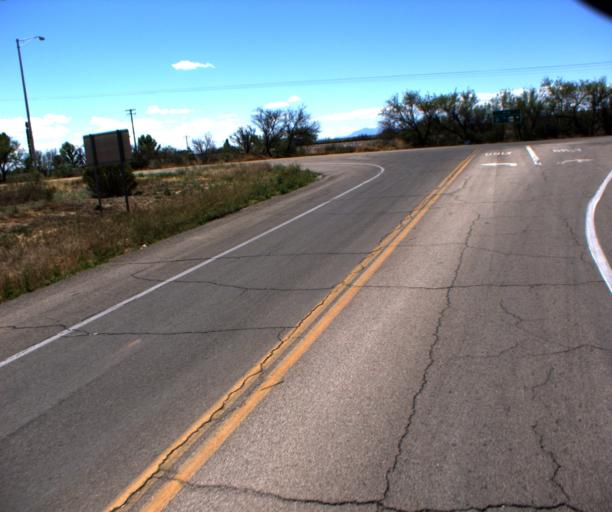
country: US
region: Arizona
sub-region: Cochise County
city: Benson
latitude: 31.9655
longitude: -110.2738
